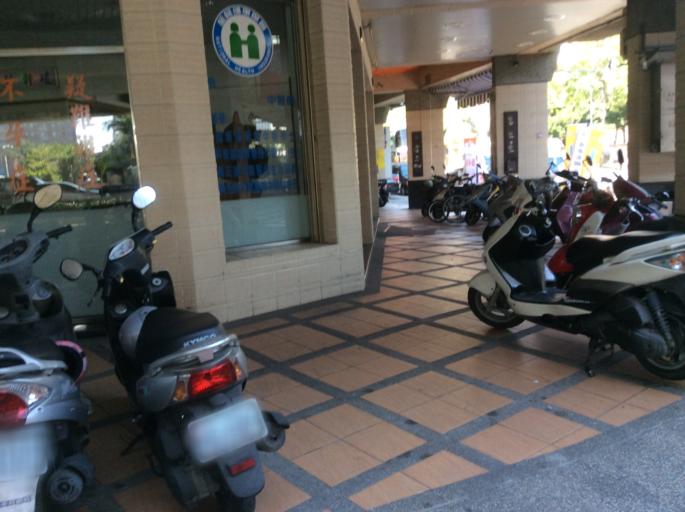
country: TW
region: Kaohsiung
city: Kaohsiung
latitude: 22.6796
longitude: 120.3134
